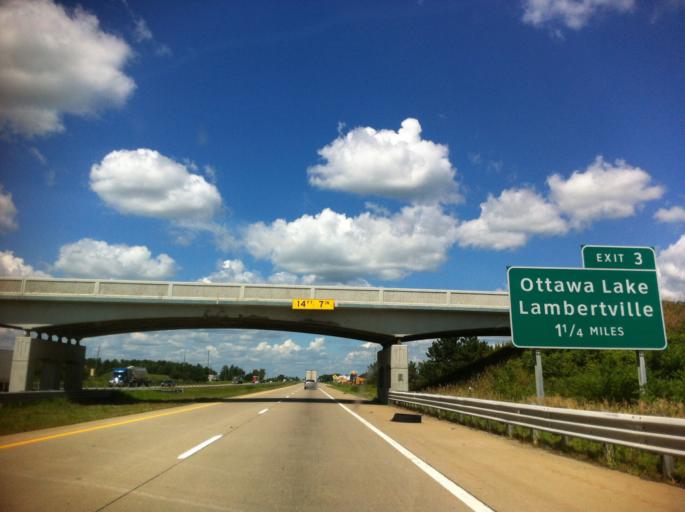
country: US
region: Ohio
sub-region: Lucas County
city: Sylvania
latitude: 41.7467
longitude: -83.6940
